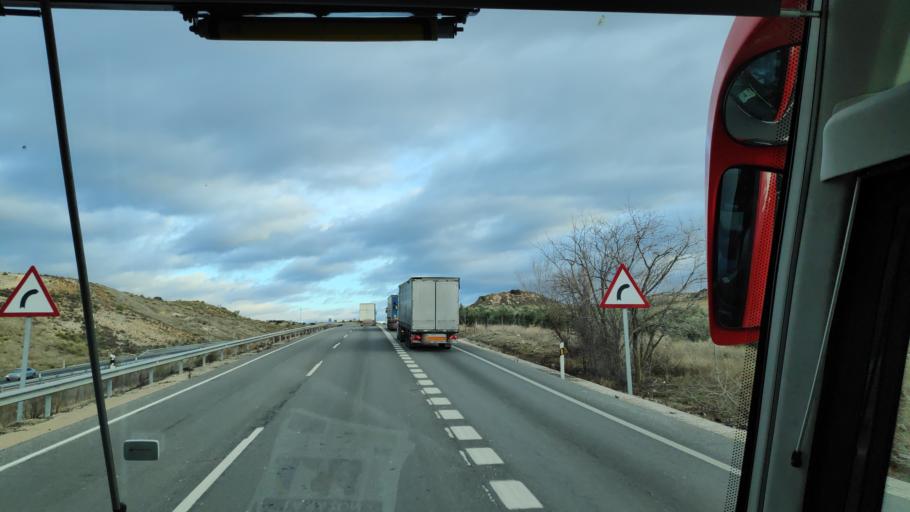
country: ES
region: Madrid
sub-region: Provincia de Madrid
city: Tielmes
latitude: 40.1984
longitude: -3.3113
